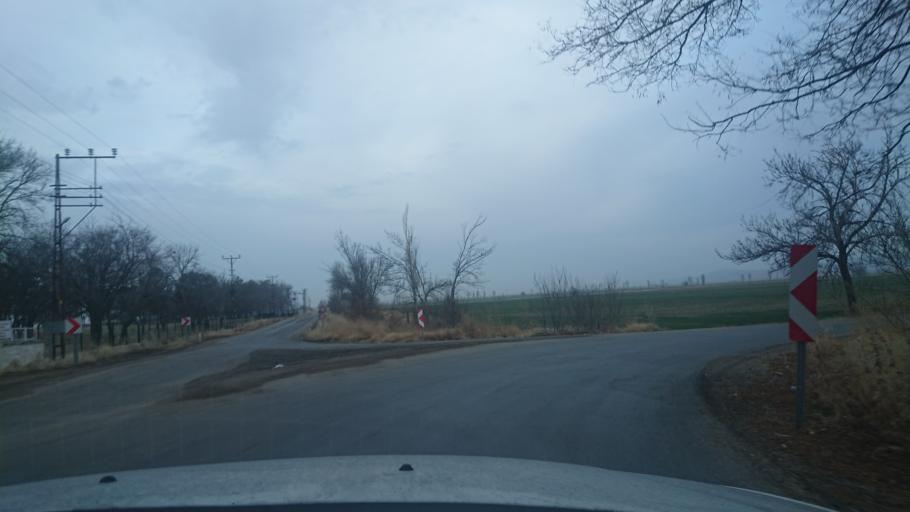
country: TR
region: Aksaray
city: Yesilova
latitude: 38.4614
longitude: 33.8410
